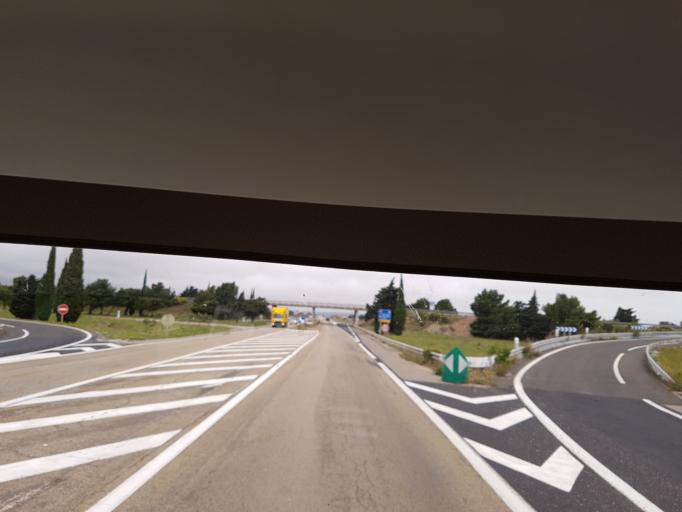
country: FR
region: Languedoc-Roussillon
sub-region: Departement de l'Aude
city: Leucate
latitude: 42.9349
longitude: 2.9917
